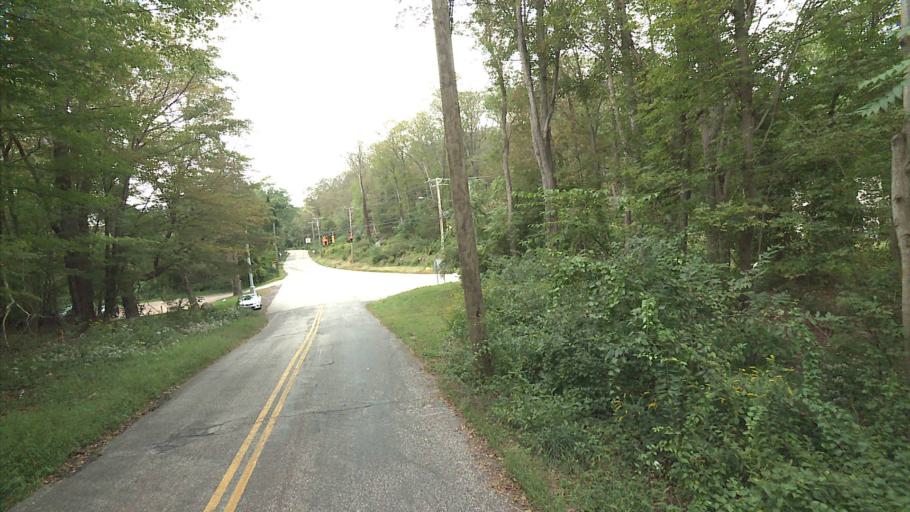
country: US
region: Connecticut
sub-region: Middlesex County
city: Higganum
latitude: 41.5296
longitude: -72.5367
